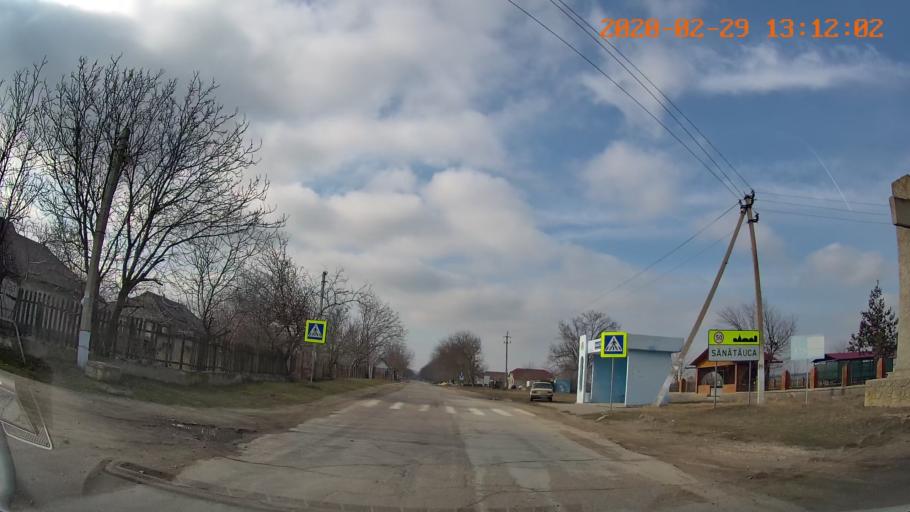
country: MD
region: Telenesti
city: Camenca
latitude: 48.0127
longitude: 28.6980
